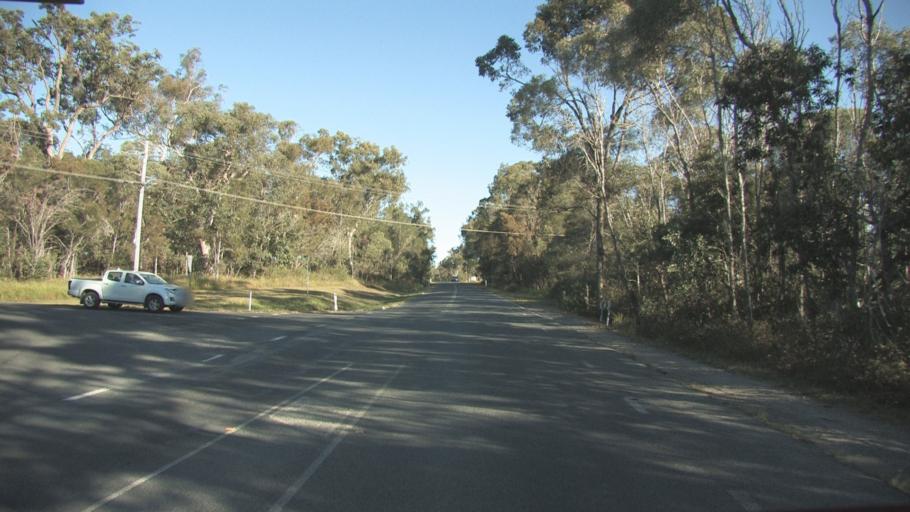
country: AU
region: Queensland
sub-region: Logan
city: Logan Reserve
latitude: -27.7234
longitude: 153.0902
